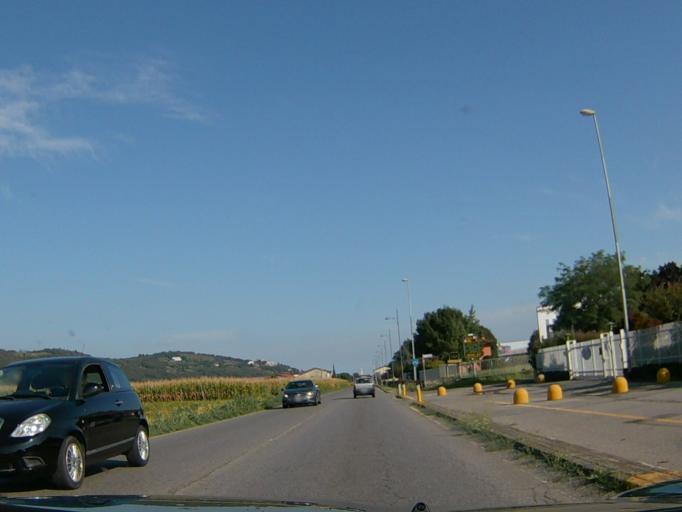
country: IT
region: Lombardy
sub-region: Provincia di Brescia
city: Cologne
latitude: 45.5737
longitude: 9.9498
